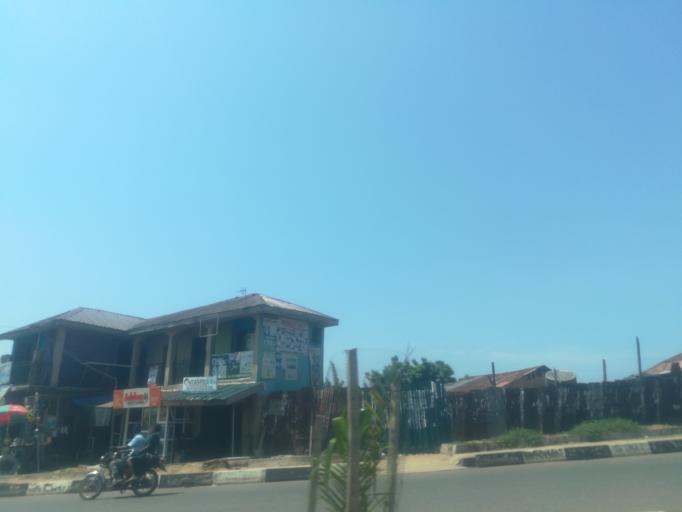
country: NG
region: Ogun
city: Abeokuta
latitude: 7.1568
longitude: 3.3493
